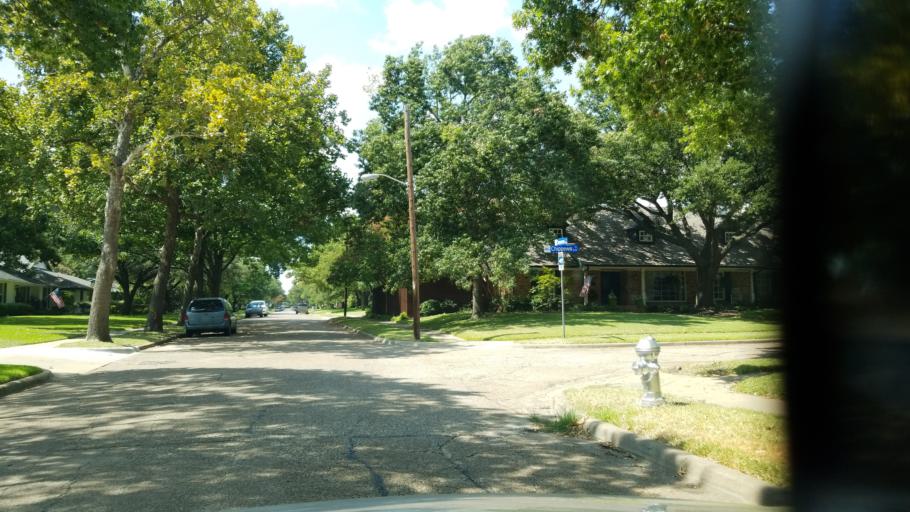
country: US
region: Texas
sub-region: Dallas County
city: Richardson
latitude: 32.9638
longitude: -96.7598
